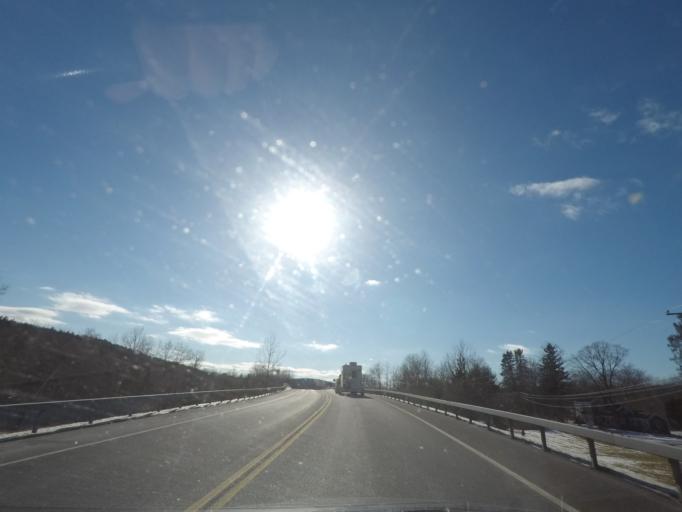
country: US
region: New York
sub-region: Columbia County
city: Chatham
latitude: 42.4192
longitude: -73.5100
